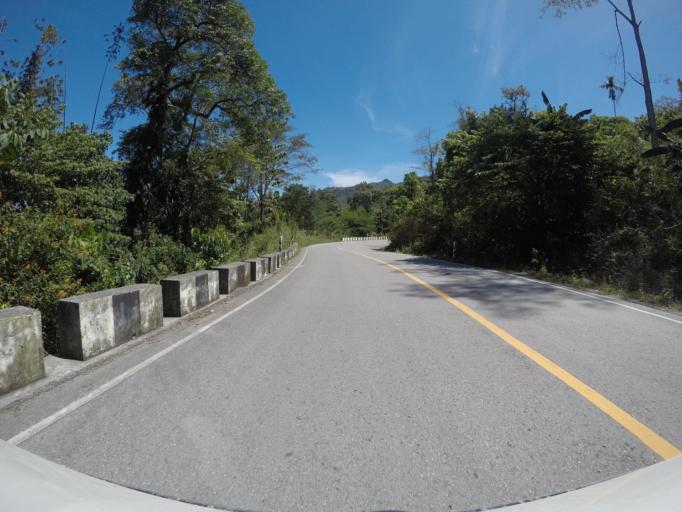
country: TL
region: Manatuto
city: Manatuto
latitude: -8.8235
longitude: 125.9793
